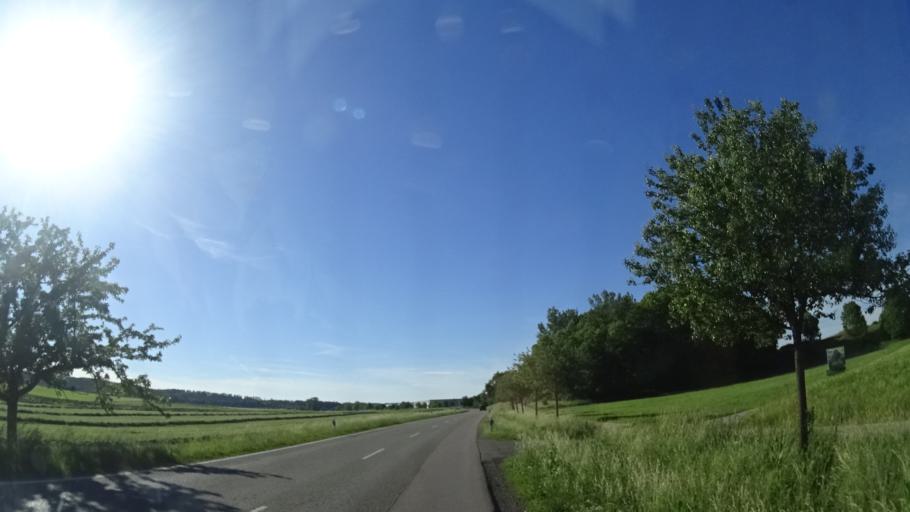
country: DE
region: Baden-Wuerttemberg
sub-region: Regierungsbezirk Stuttgart
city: Buhlertann
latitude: 49.0446
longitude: 9.8972
